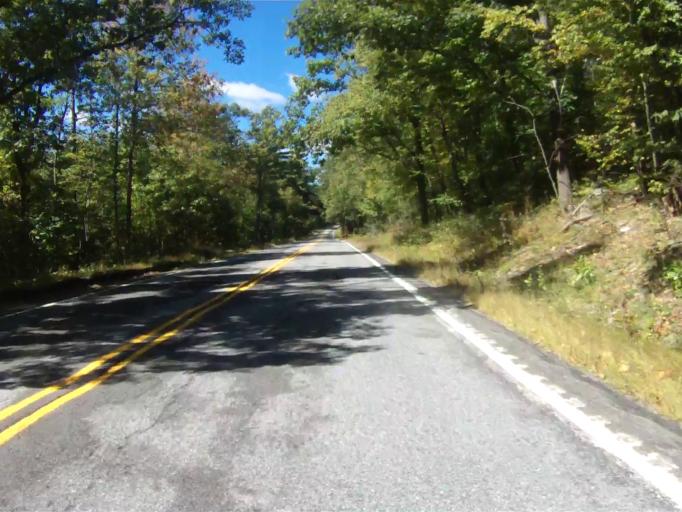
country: US
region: Pennsylvania
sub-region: Centre County
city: Park Forest Village
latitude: 40.9237
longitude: -77.9554
